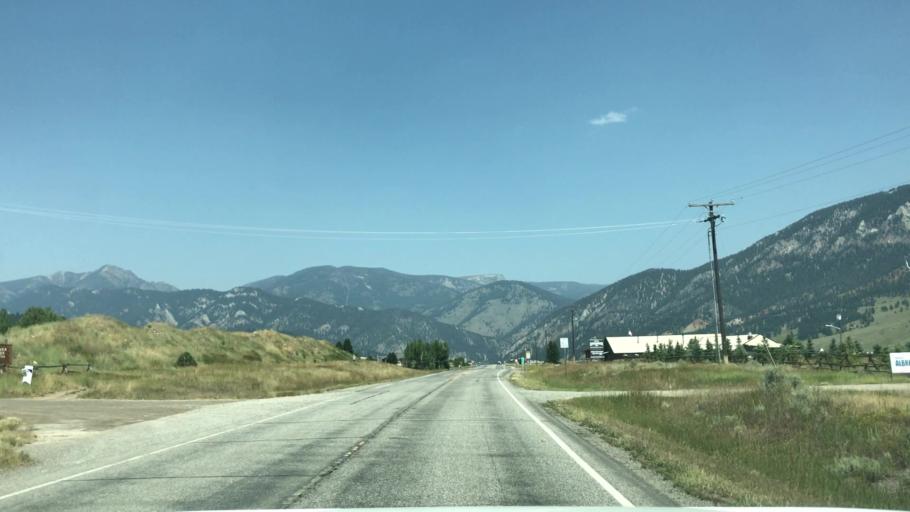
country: US
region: Montana
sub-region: Gallatin County
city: Big Sky
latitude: 45.2223
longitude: -111.2508
